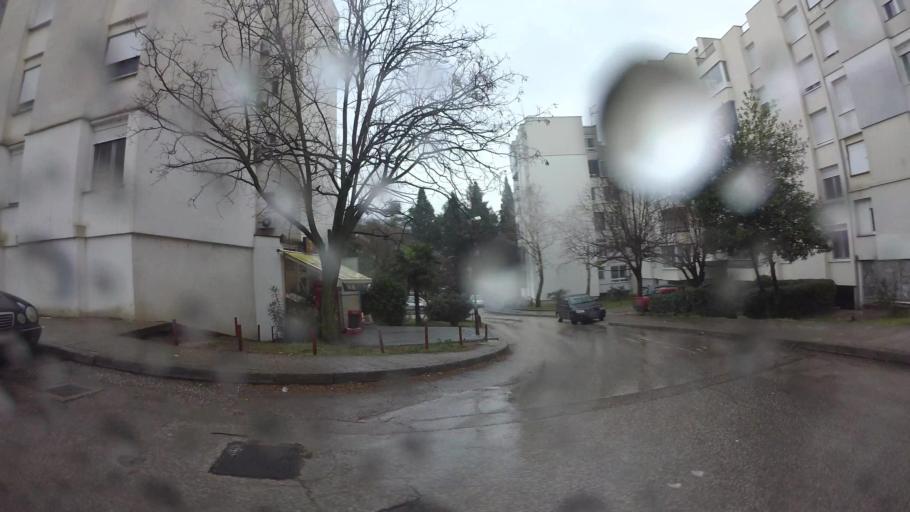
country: BA
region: Federation of Bosnia and Herzegovina
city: Cim
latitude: 43.3457
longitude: 17.7926
